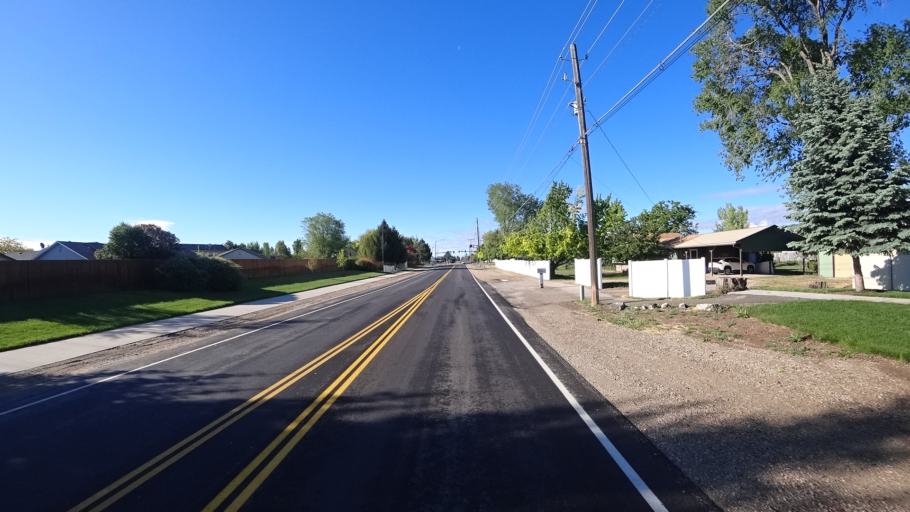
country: US
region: Idaho
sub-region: Ada County
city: Kuna
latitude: 43.5068
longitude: -116.4138
